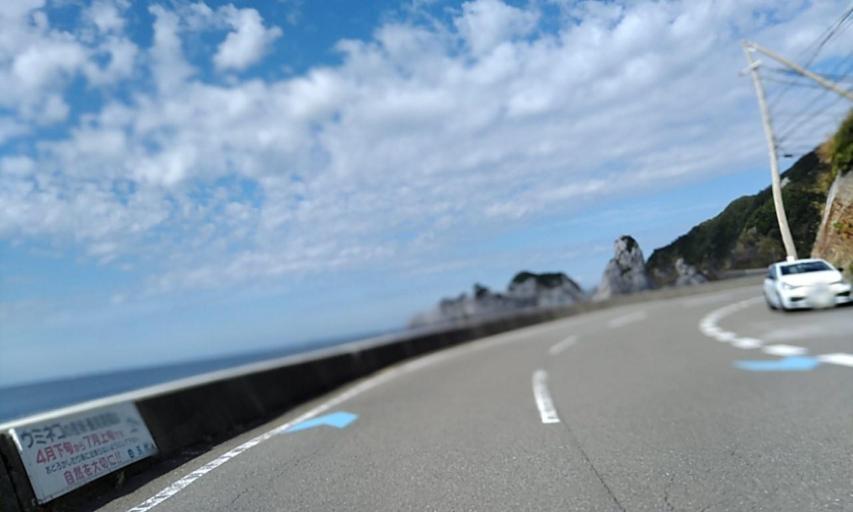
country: JP
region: Wakayama
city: Gobo
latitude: 33.9698
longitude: 135.0794
